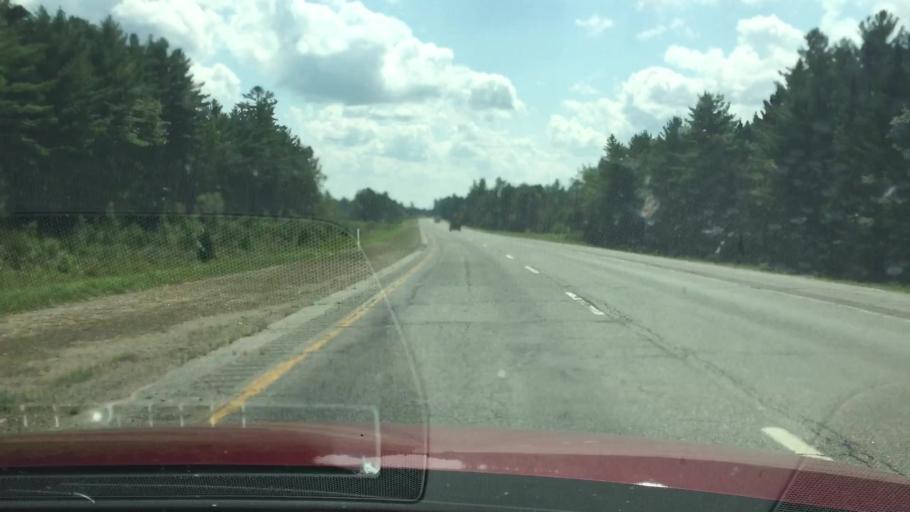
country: US
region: Maine
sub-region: Penobscot County
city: Medway
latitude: 45.5886
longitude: -68.5428
